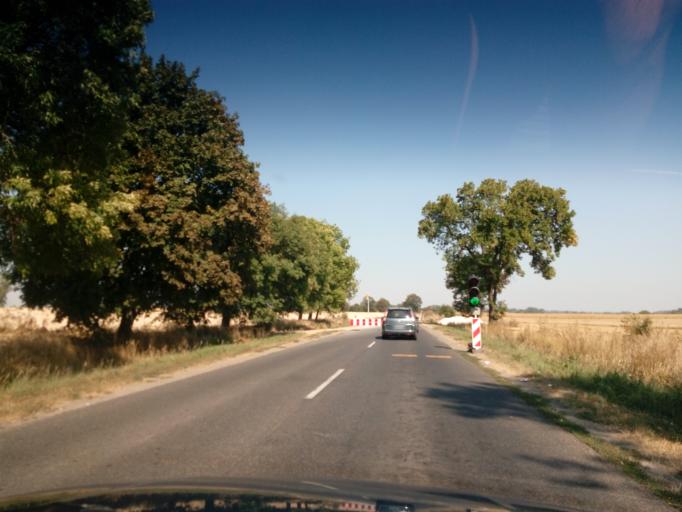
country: PL
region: Lublin Voivodeship
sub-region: Powiat hrubieszowski
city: Hrubieszow
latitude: 50.8266
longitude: 23.9513
